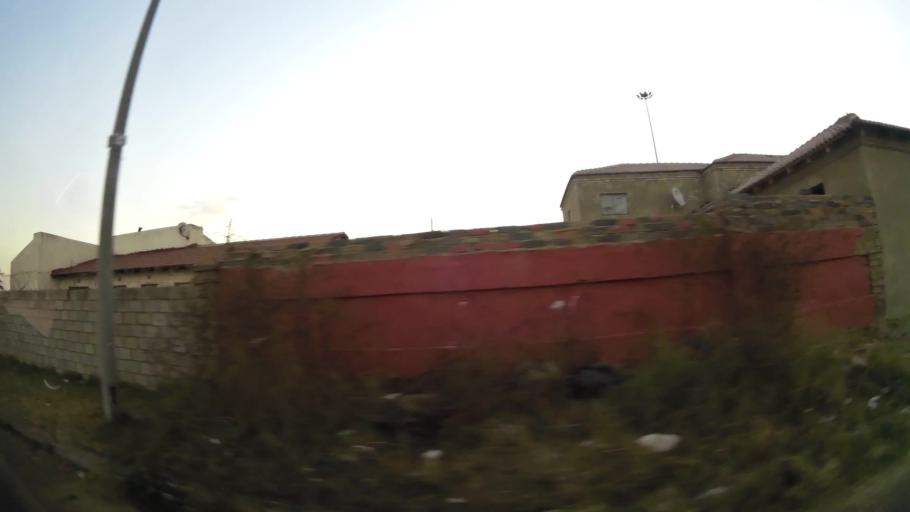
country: ZA
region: Gauteng
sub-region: West Rand District Municipality
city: Randfontein
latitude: -26.2118
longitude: 27.7141
